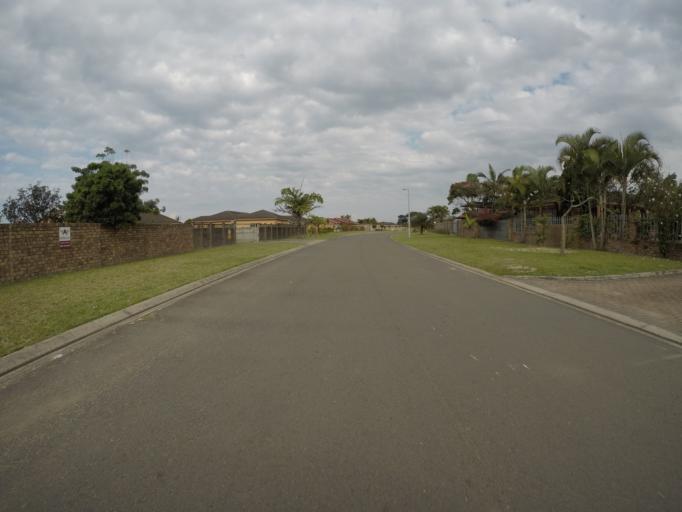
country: ZA
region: KwaZulu-Natal
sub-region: uThungulu District Municipality
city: Richards Bay
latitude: -28.7343
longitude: 32.0902
